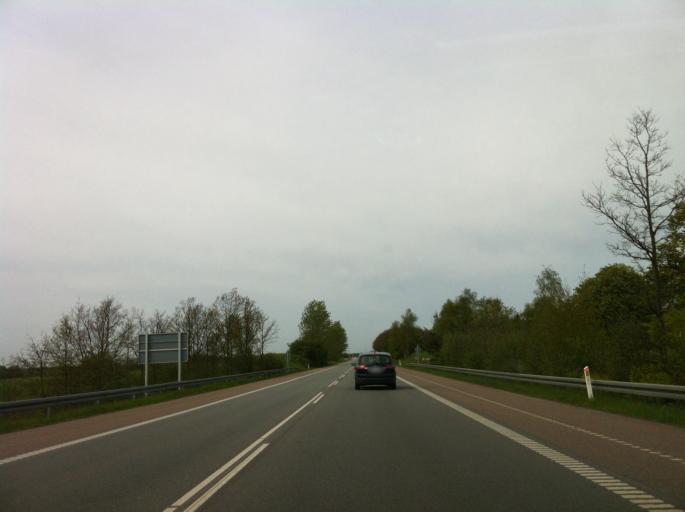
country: DK
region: Capital Region
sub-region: Hillerod Kommune
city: Hillerod
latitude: 55.9062
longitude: 12.2824
